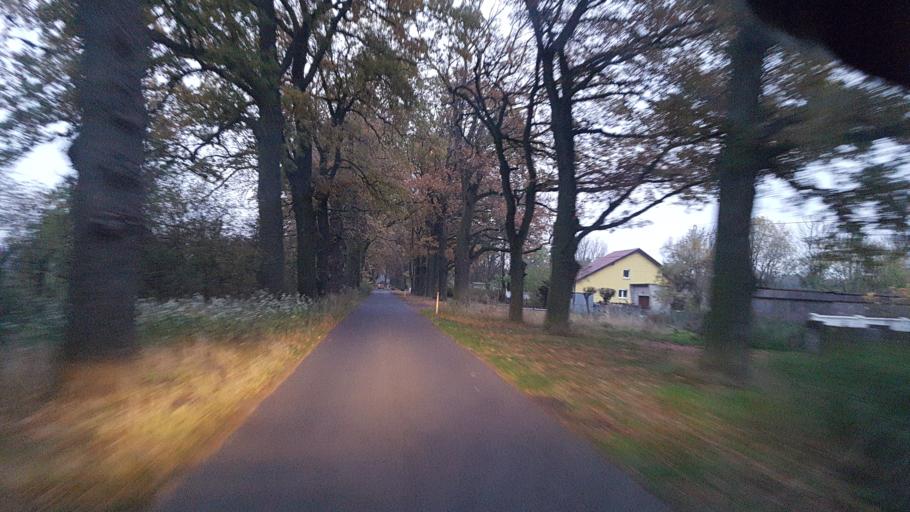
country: DE
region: Brandenburg
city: Nauen
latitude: 52.6403
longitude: 12.8992
